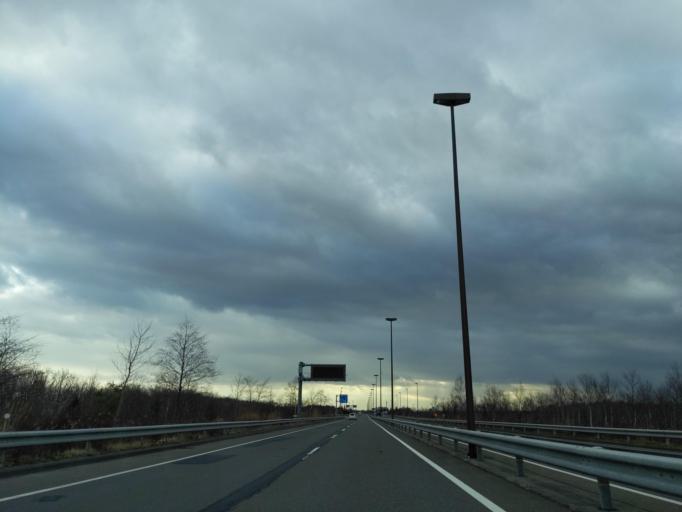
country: JP
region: Hokkaido
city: Chitose
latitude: 42.8231
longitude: 141.6860
